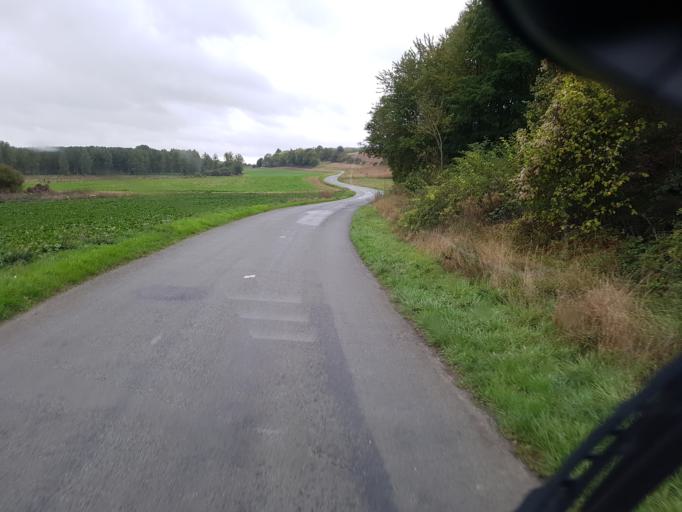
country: FR
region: Picardie
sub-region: Departement de l'Oise
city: Breteuil
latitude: 49.6798
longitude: 2.3301
